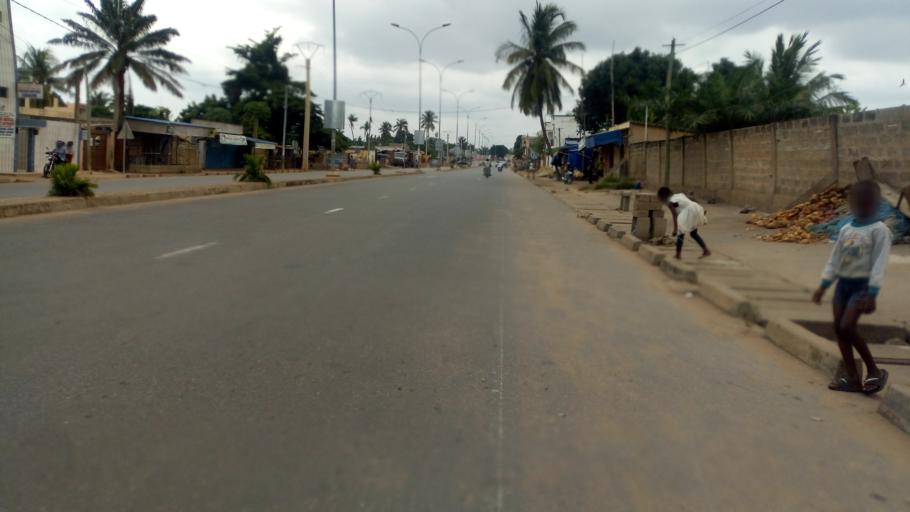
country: TG
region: Maritime
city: Lome
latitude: 6.2074
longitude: 1.1887
